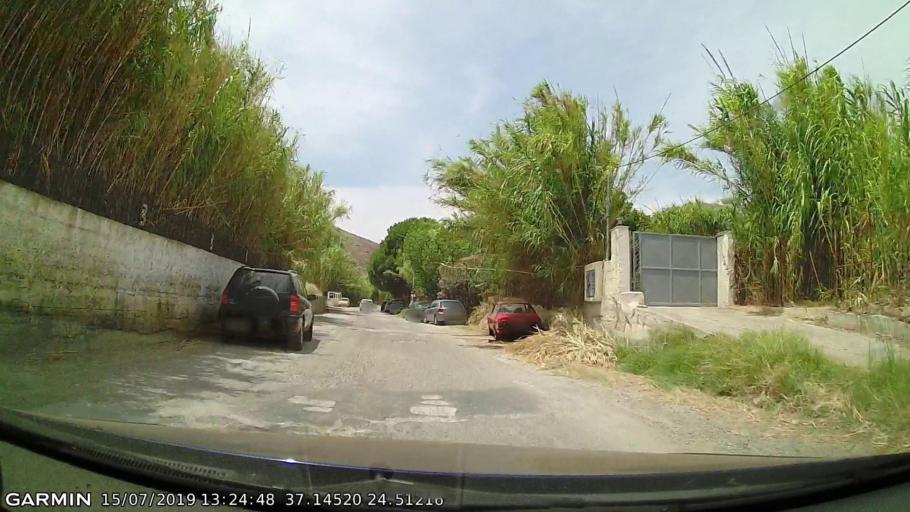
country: GR
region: South Aegean
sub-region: Nomos Kykladon
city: Serifos
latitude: 37.1452
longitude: 24.5122
